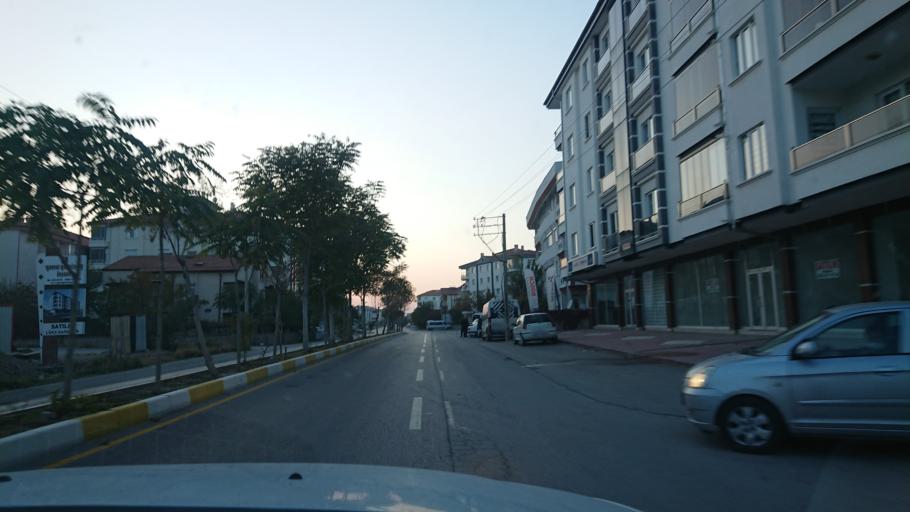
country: TR
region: Aksaray
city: Aksaray
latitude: 38.3604
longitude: 34.0143
